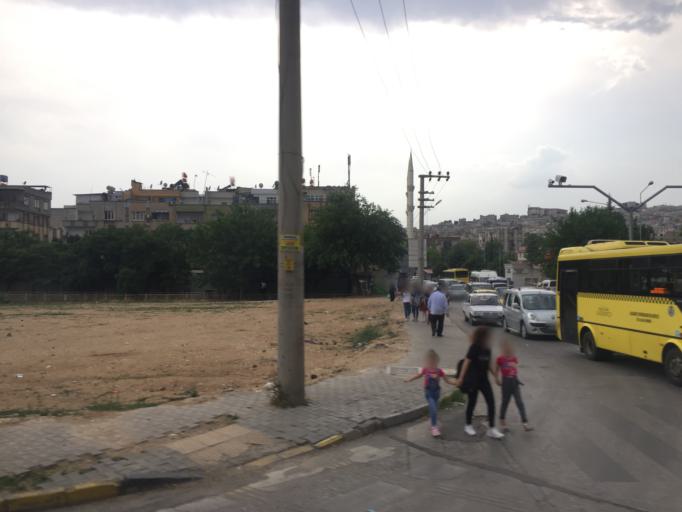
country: TR
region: Gaziantep
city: Gaziantep
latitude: 37.0672
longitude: 37.4142
